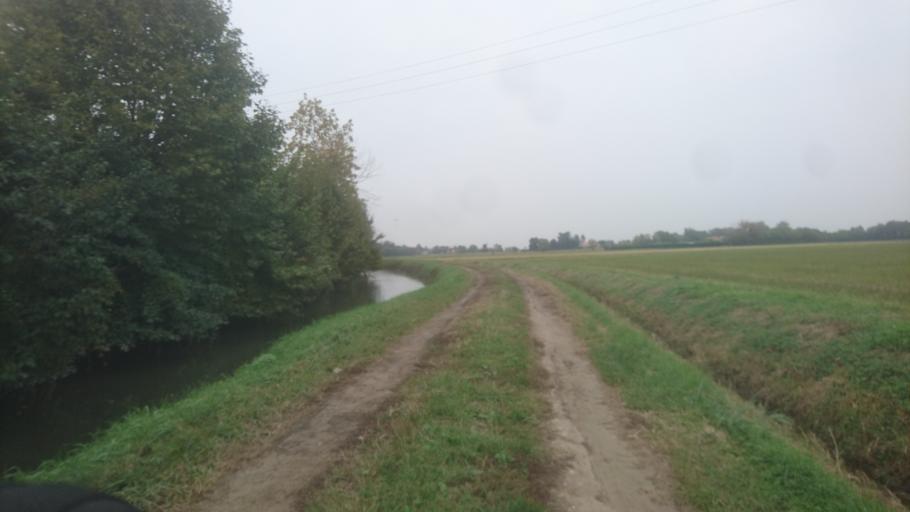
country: IT
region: Veneto
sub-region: Provincia di Vicenza
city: Grumolo delle Abbadesse
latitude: 45.5485
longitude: 11.6730
